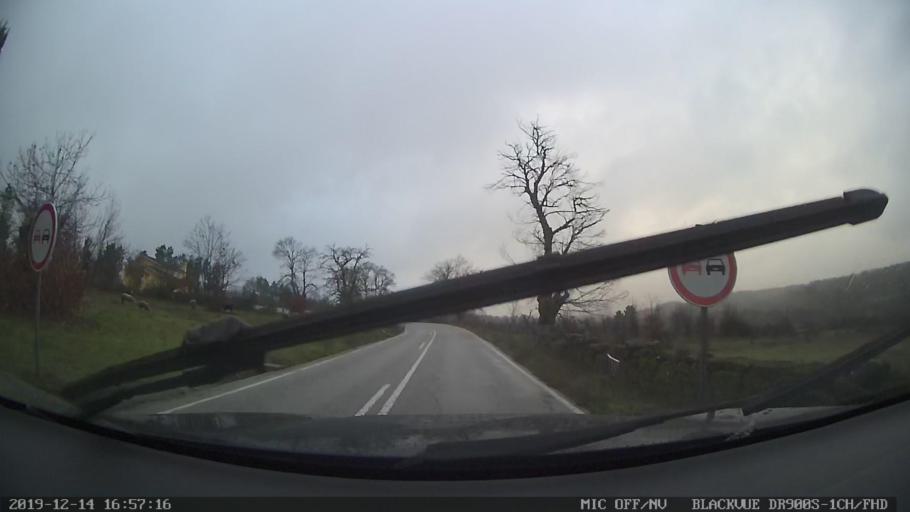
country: PT
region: Vila Real
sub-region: Murca
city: Murca
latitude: 41.4361
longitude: -7.5444
